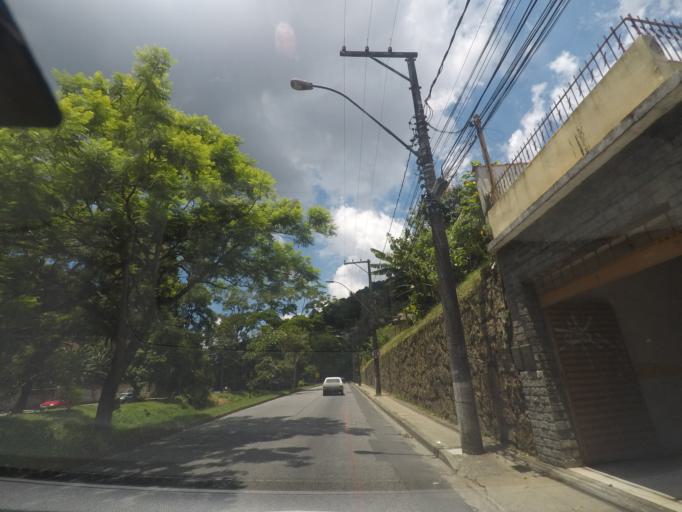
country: BR
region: Rio de Janeiro
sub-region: Petropolis
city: Petropolis
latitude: -22.4965
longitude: -43.1803
